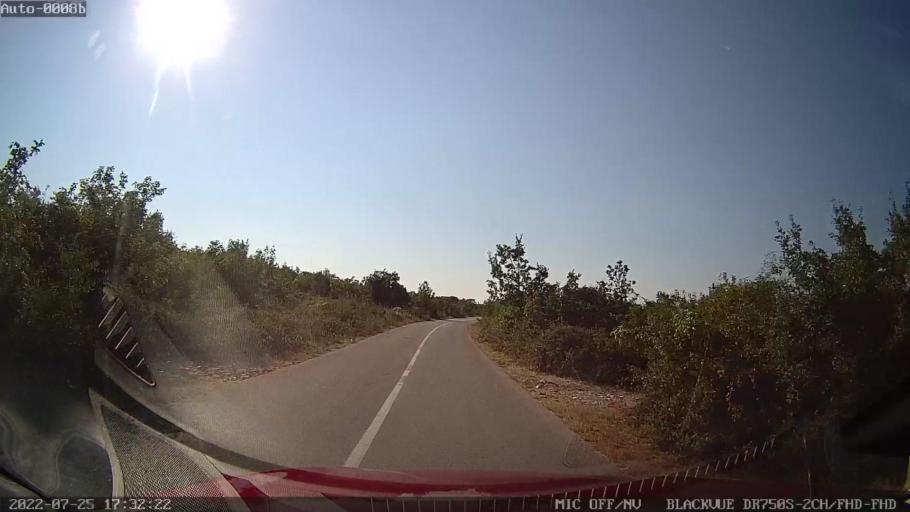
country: HR
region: Zadarska
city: Posedarje
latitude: 44.1761
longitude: 15.4938
